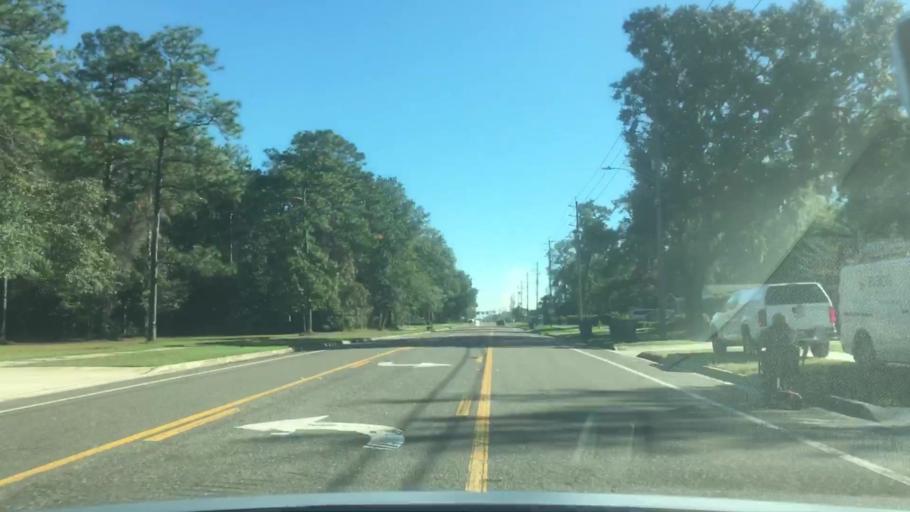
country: US
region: Florida
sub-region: Duval County
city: Jacksonville
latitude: 30.4298
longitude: -81.6773
